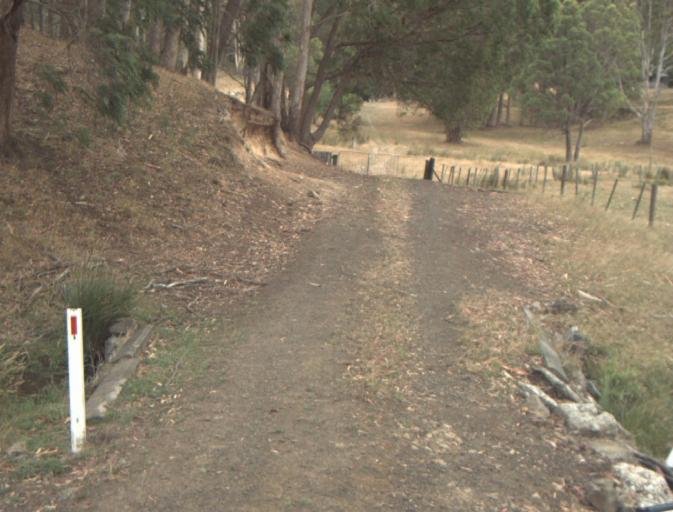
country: AU
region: Tasmania
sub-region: Dorset
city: Scottsdale
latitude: -41.4516
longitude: 147.6012
